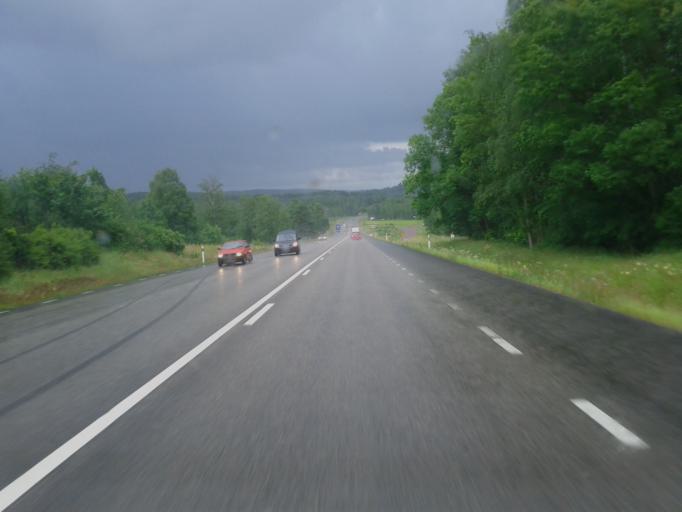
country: SE
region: Dalarna
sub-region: Rattviks Kommun
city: Vikarbyn
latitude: 60.9130
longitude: 15.0280
